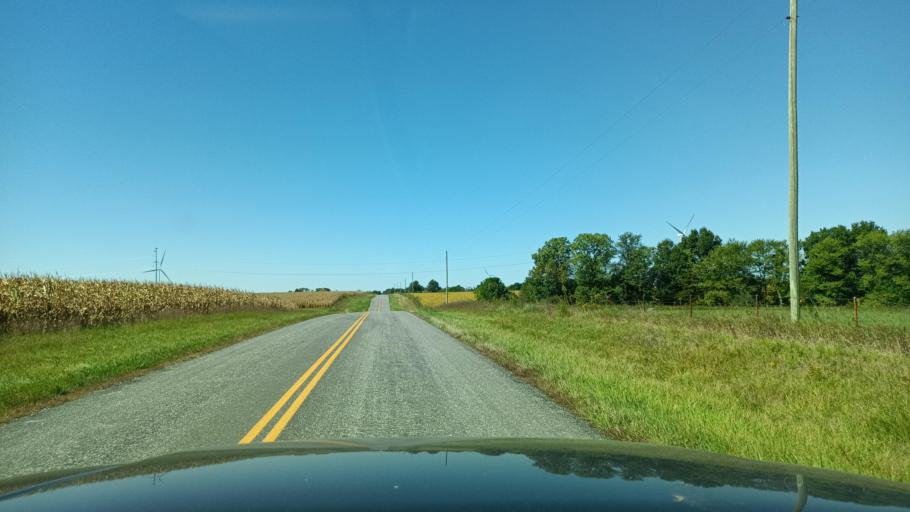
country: US
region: Missouri
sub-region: Adair County
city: Kirksville
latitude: 40.3307
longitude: -92.4871
